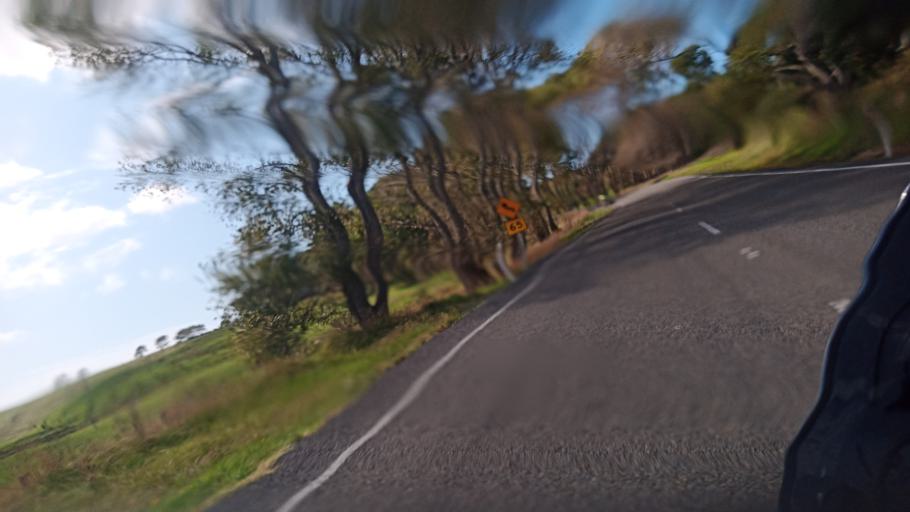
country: NZ
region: Gisborne
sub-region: Gisborne District
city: Gisborne
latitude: -38.5497
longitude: 178.2182
